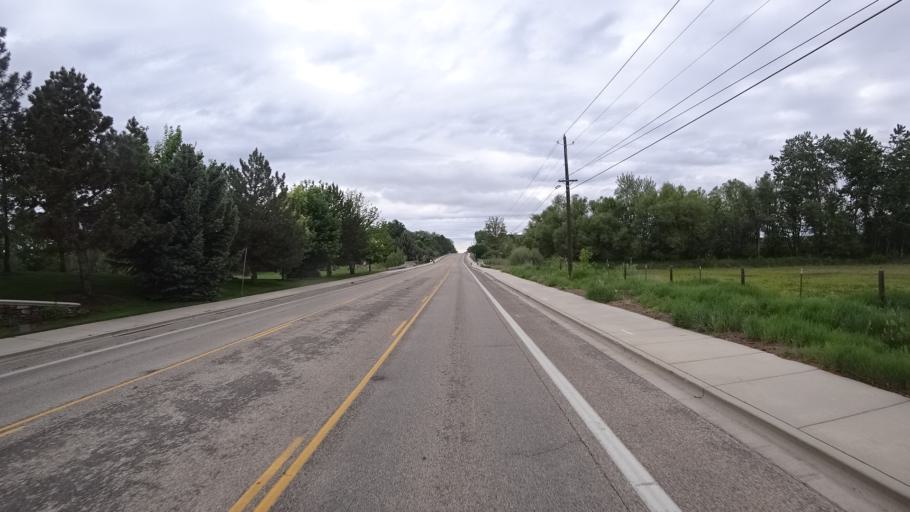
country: US
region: Idaho
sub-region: Ada County
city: Eagle
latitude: 43.7064
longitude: -116.3568
